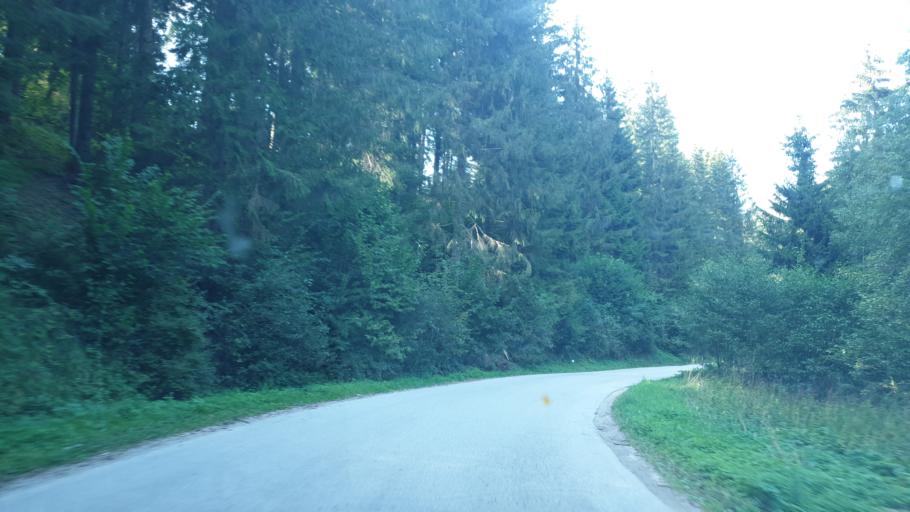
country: RS
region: Central Serbia
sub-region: Zlatiborski Okrug
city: Nova Varos
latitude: 43.4541
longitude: 19.8421
